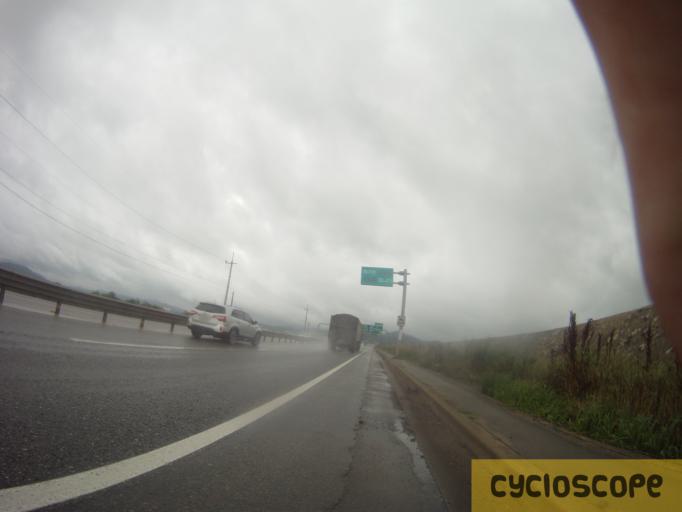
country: KR
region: Gyeonggi-do
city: Hwaseong-si
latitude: 36.9977
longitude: 126.8389
